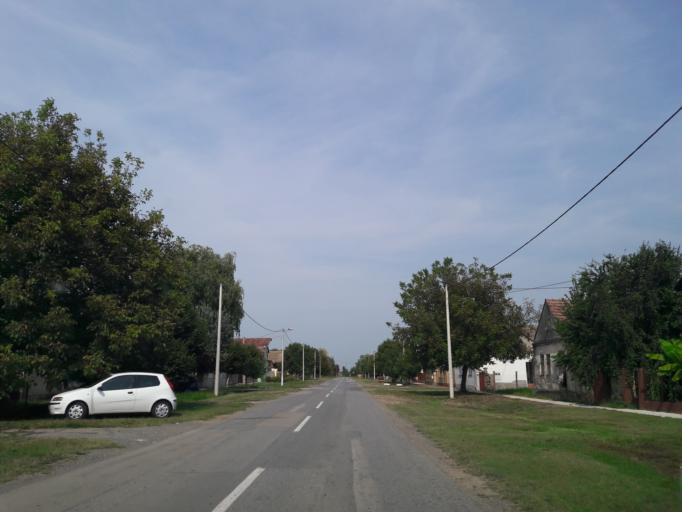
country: HR
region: Vukovarsko-Srijemska
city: Nustar
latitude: 45.3730
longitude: 18.8484
